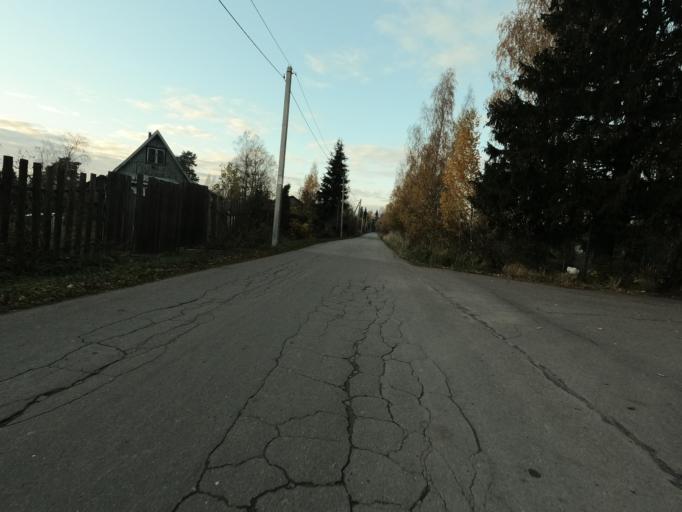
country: RU
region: Leningrad
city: Mga
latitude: 59.7781
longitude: 31.2052
